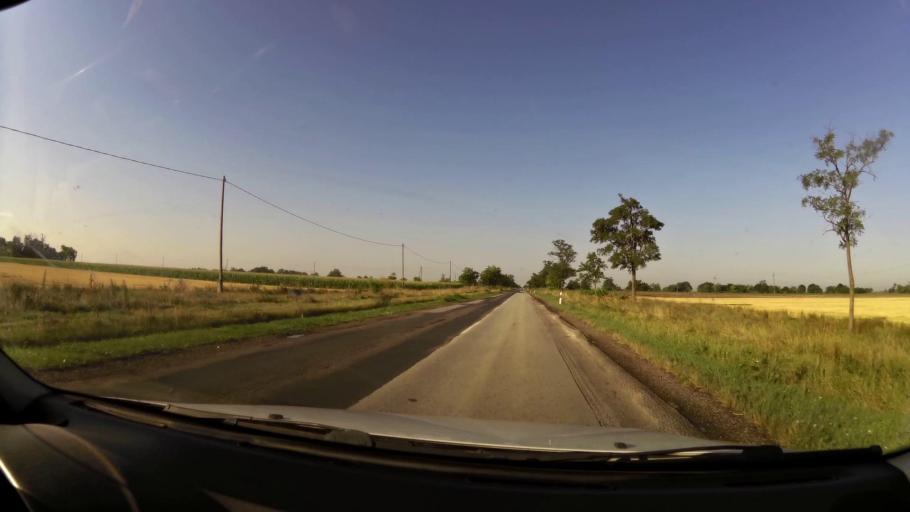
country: HU
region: Pest
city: Cegled
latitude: 47.2160
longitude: 19.8258
